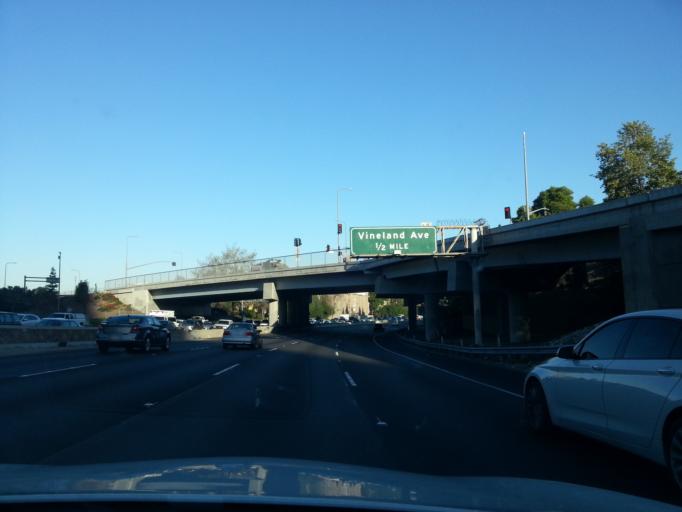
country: US
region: California
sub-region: Los Angeles County
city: Universal City
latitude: 34.1392
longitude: -118.3647
